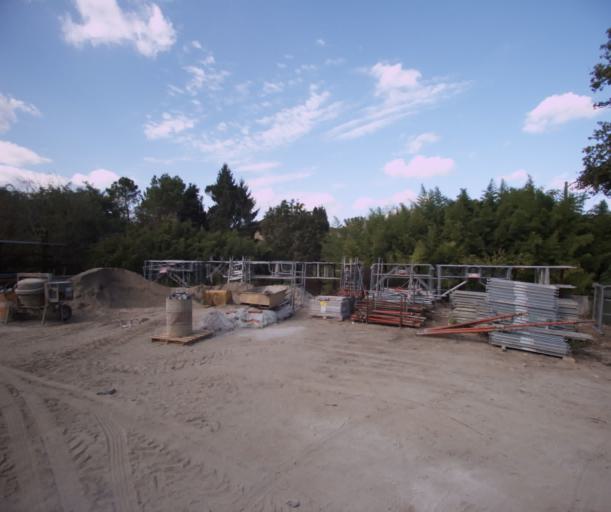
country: FR
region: Midi-Pyrenees
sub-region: Departement du Gers
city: Cazaubon
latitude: 43.9371
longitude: -0.0719
